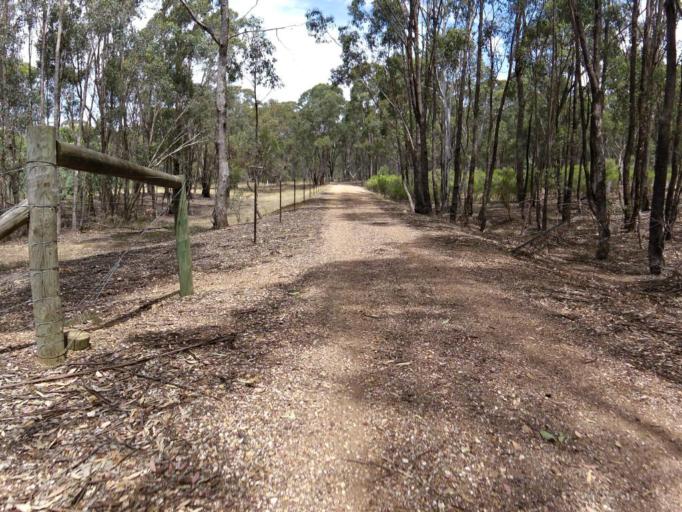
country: AU
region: Victoria
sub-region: Greater Bendigo
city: Kennington
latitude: -36.8845
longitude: 144.6554
